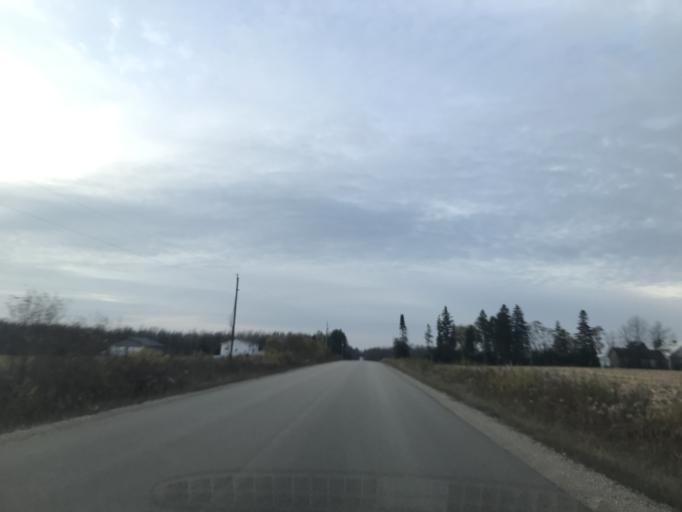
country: US
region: Wisconsin
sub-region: Marinette County
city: Peshtigo
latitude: 45.0803
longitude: -87.7996
